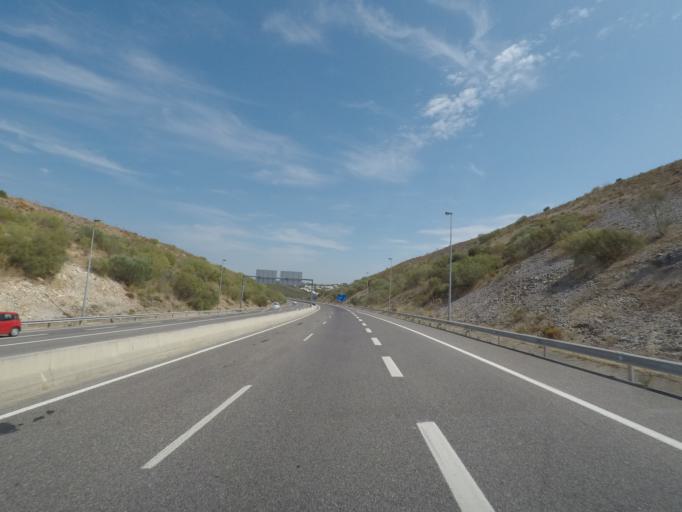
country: PT
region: Faro
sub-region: Lagos
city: Lagos
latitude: 37.1420
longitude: -8.7151
